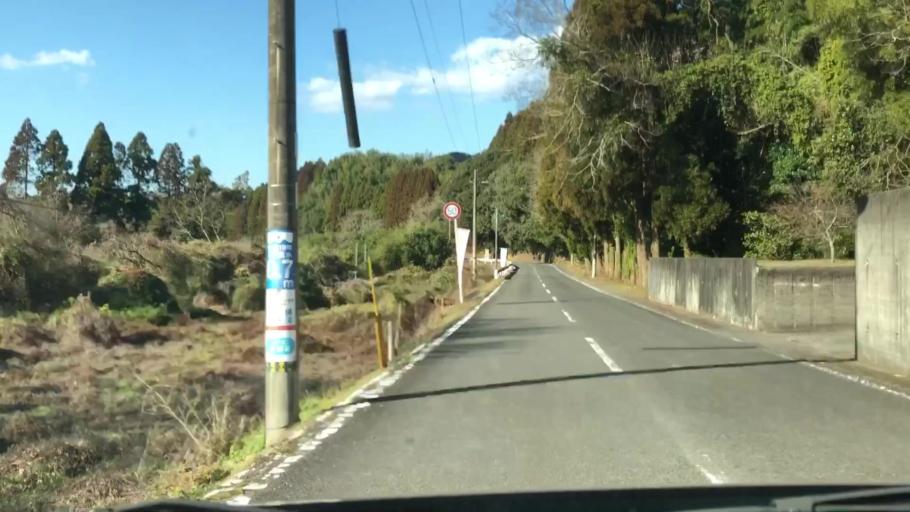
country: JP
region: Kagoshima
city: Satsumasendai
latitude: 31.8563
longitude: 130.3606
